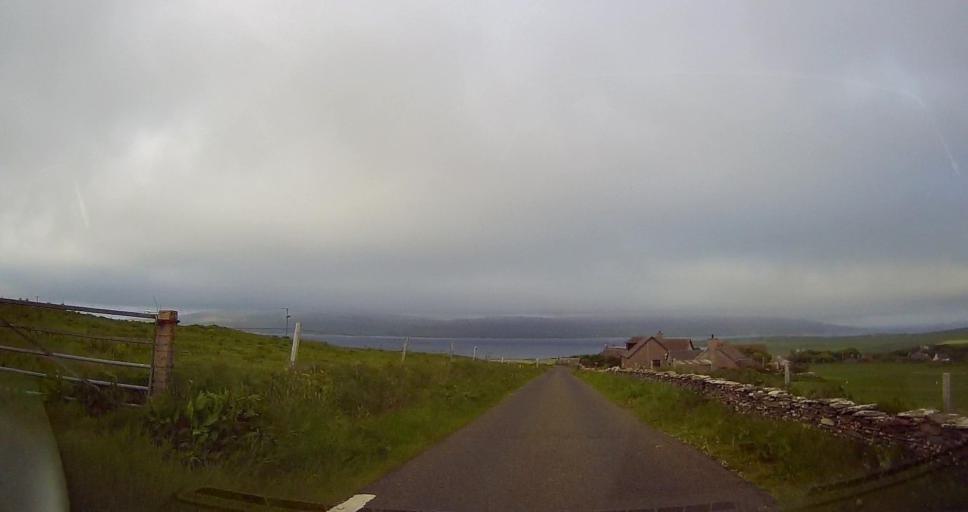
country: GB
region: Scotland
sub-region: Orkney Islands
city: Orkney
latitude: 59.1127
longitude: -3.1147
